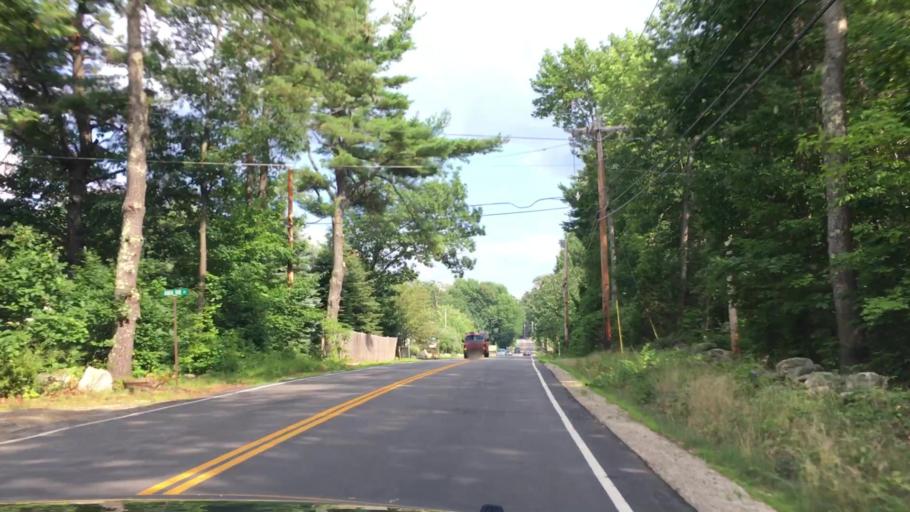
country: US
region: New Hampshire
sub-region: Belknap County
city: Gilford
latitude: 43.5576
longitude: -71.3243
